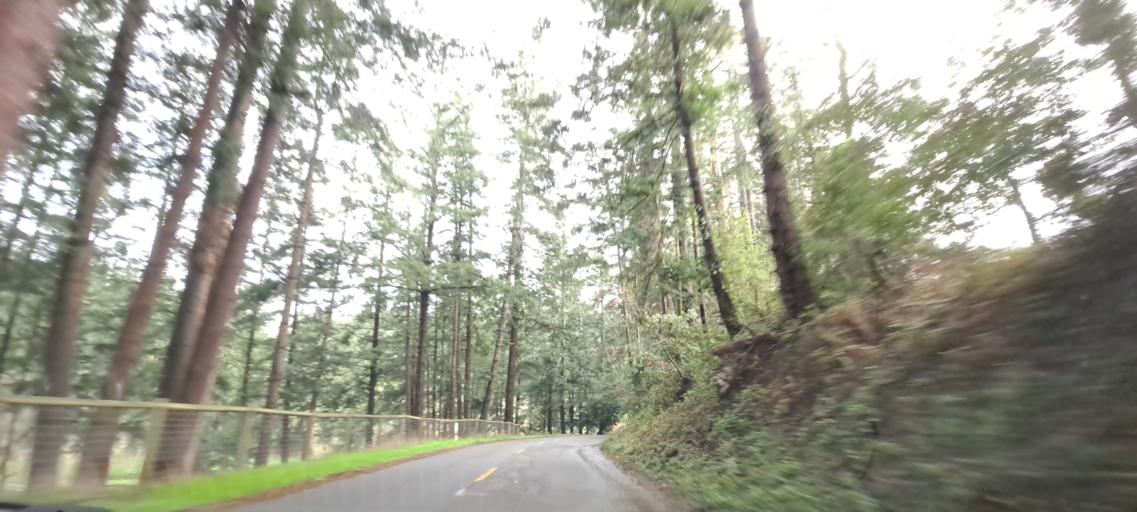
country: US
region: California
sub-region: Humboldt County
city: Fortuna
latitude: 40.6005
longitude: -124.1401
